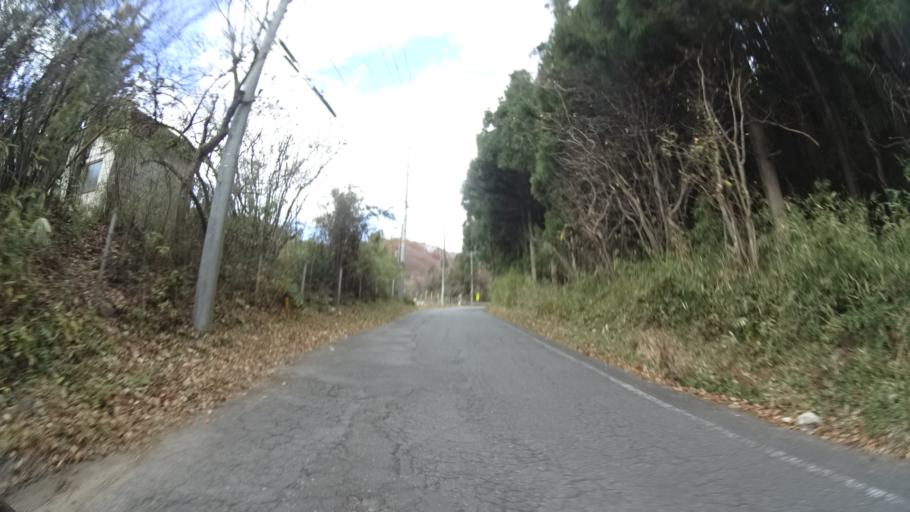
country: JP
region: Gunma
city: Omamacho-omama
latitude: 36.4910
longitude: 139.1851
